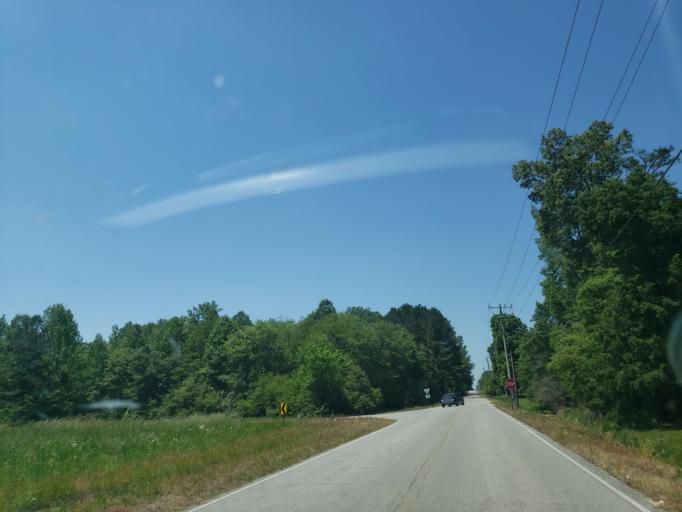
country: US
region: Alabama
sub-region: Madison County
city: Harvest
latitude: 34.9625
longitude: -86.7122
